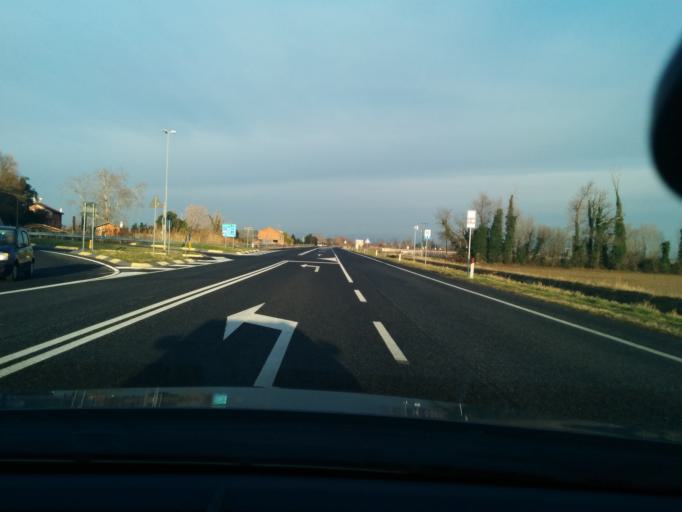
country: IT
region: Friuli Venezia Giulia
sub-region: Provincia di Gorizia
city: San Canzian d'Isonzo
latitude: 45.7460
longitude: 13.4479
